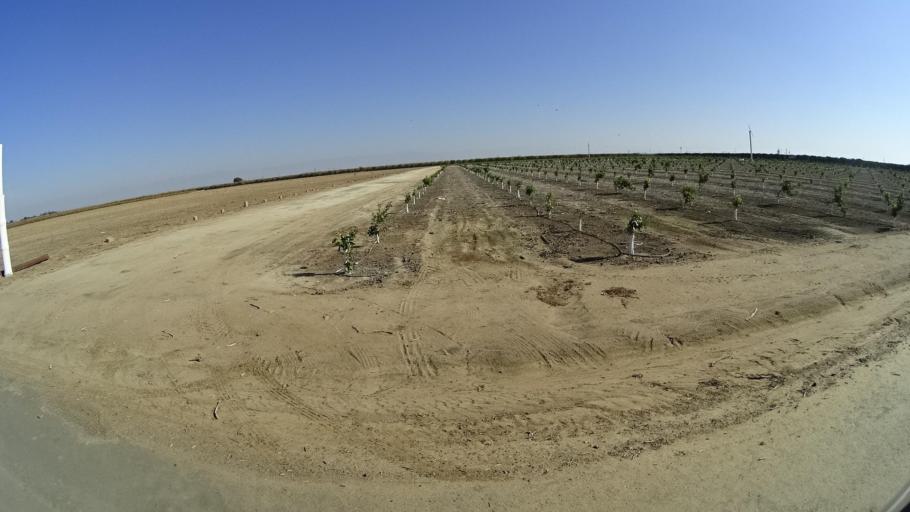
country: US
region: California
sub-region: Tulare County
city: Richgrove
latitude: 35.7380
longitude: -119.1430
